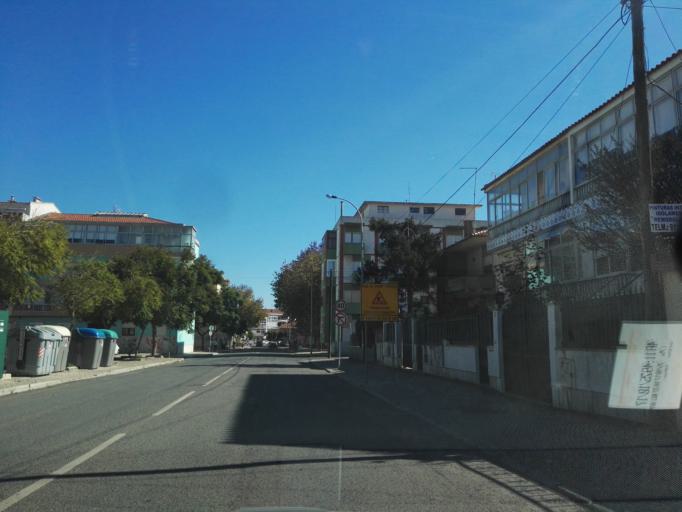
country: PT
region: Lisbon
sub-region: Sintra
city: Sintra
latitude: 38.7974
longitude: -9.3498
